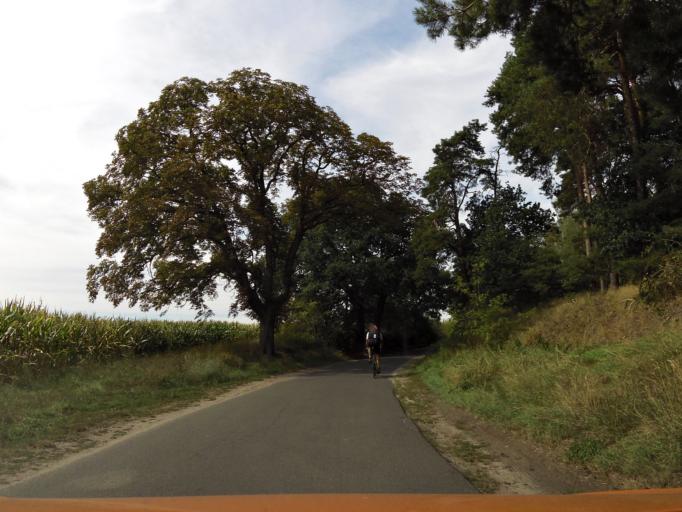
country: DE
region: Brandenburg
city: Michendorf
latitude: 52.2406
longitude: 13.0930
